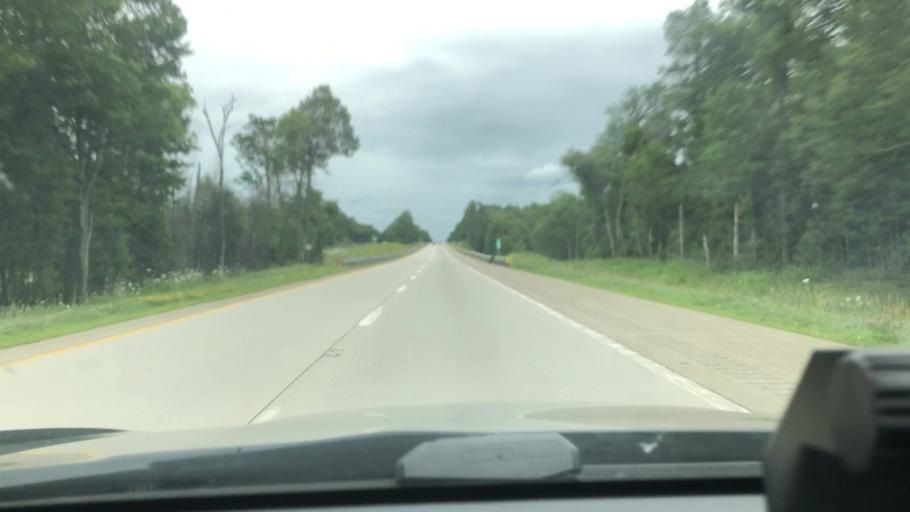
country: US
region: Pennsylvania
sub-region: Monroe County
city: Pocono Pines
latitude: 41.1639
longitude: -75.4215
